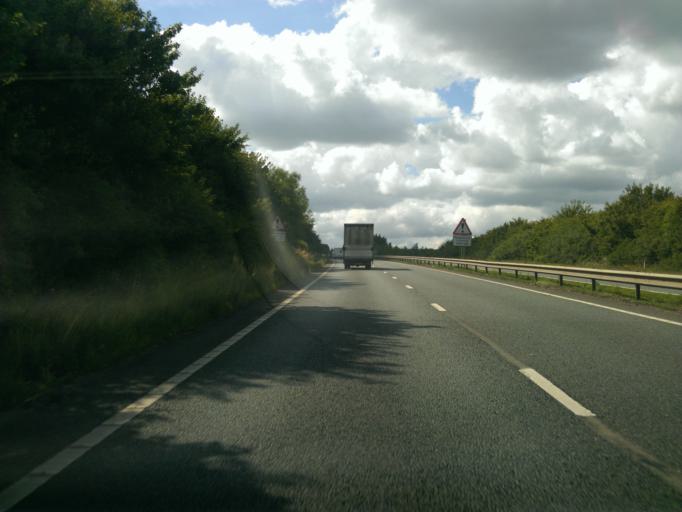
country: GB
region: England
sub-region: Leicestershire
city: Market Harborough
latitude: 52.4059
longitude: -0.9453
